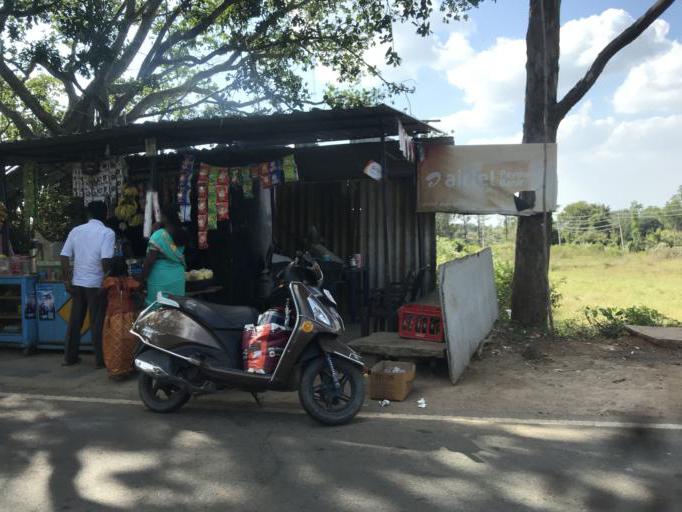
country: IN
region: Karnataka
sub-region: Bangalore Urban
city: Anekal
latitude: 12.8035
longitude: 77.5602
